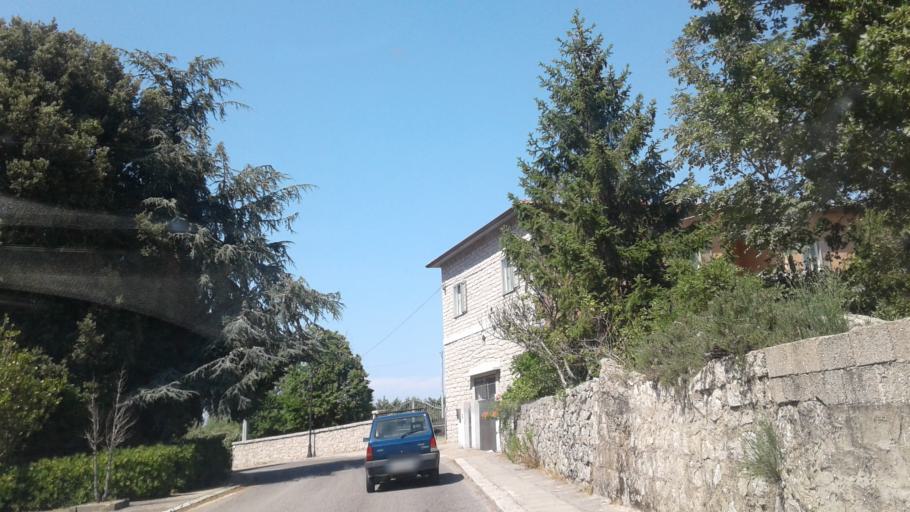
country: IT
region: Sardinia
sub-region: Provincia di Olbia-Tempio
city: Aggius
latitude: 40.9329
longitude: 9.0671
